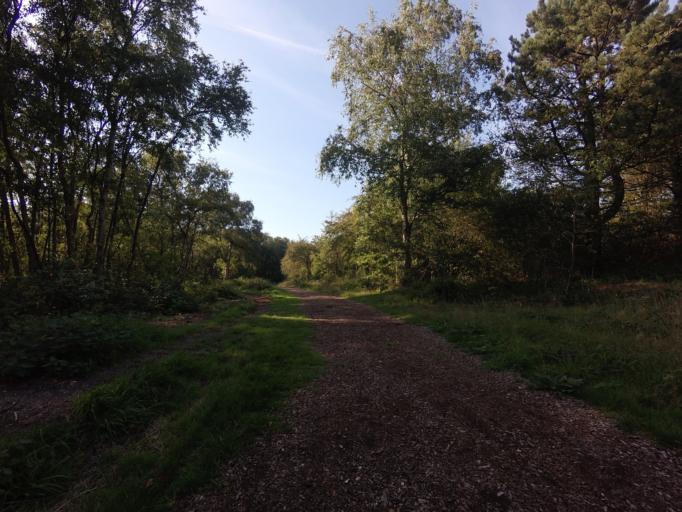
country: NL
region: Friesland
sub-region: Gemeente Schiermonnikoog
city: Schiermonnikoog
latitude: 53.4889
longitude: 6.1739
